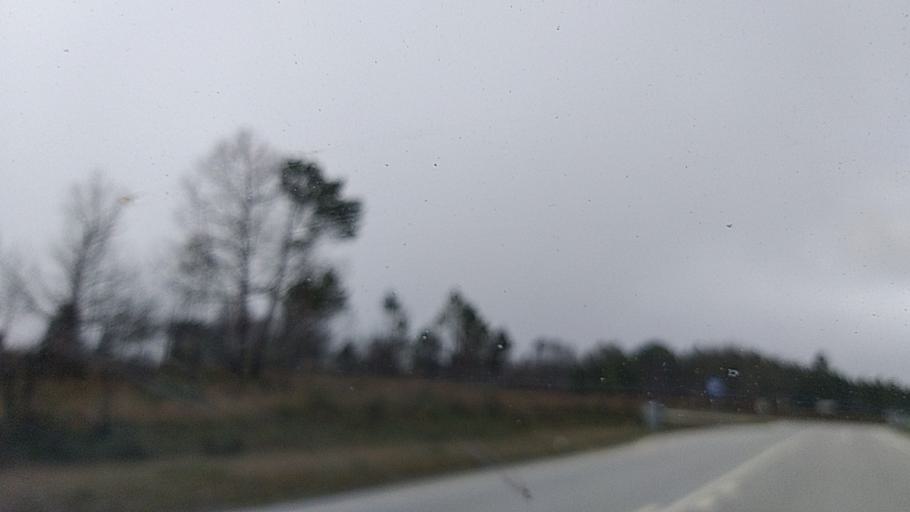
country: PT
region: Guarda
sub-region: Fornos de Algodres
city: Fornos de Algodres
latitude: 40.6919
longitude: -7.4697
